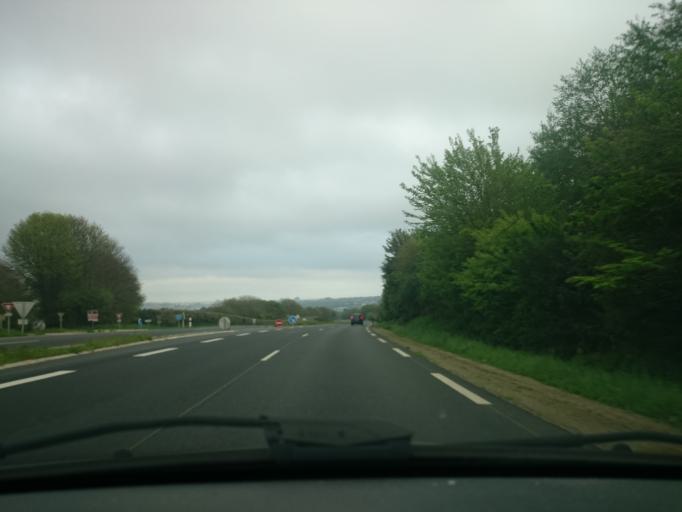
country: FR
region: Brittany
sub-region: Departement du Finistere
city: Guilers
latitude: 48.4165
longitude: -4.5457
